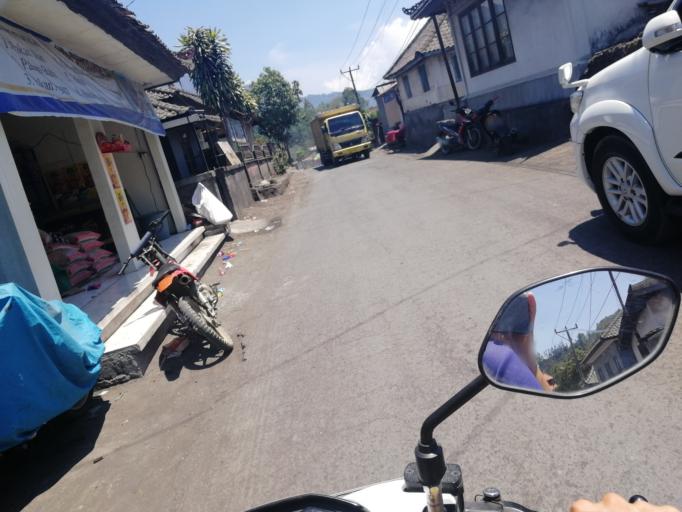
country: ID
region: Bali
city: Banjar Trunyan
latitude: -8.2275
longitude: 115.4095
